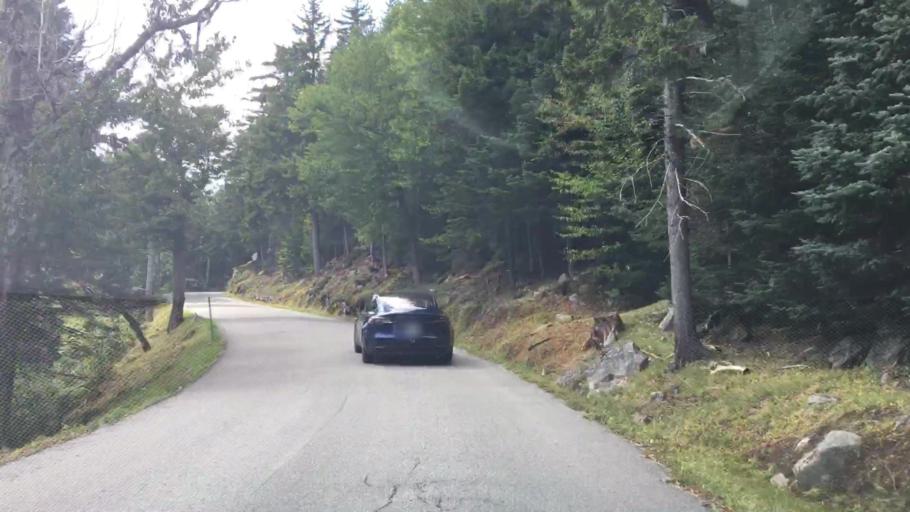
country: US
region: New Hampshire
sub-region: Coos County
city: Gorham
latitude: 44.2813
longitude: -71.2539
